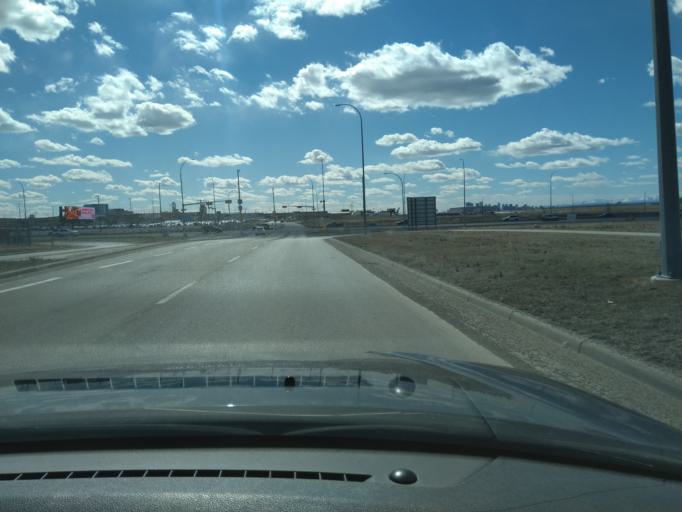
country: CA
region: Alberta
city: Calgary
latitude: 51.1408
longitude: -114.0134
